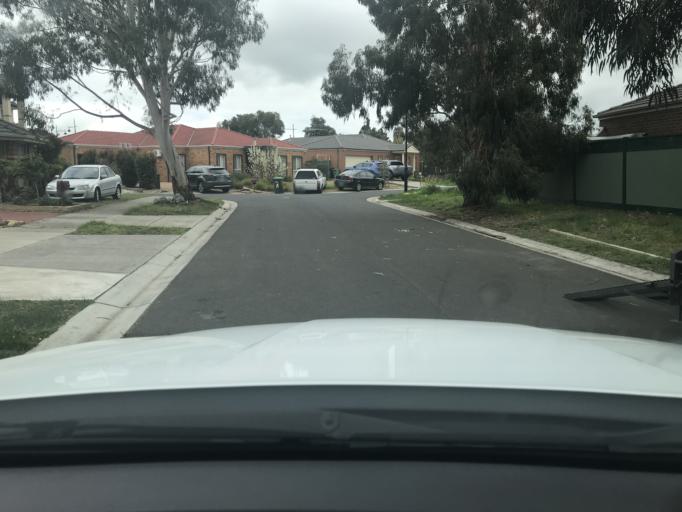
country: AU
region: Victoria
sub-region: Hume
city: Craigieburn
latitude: -37.5834
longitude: 144.9218
